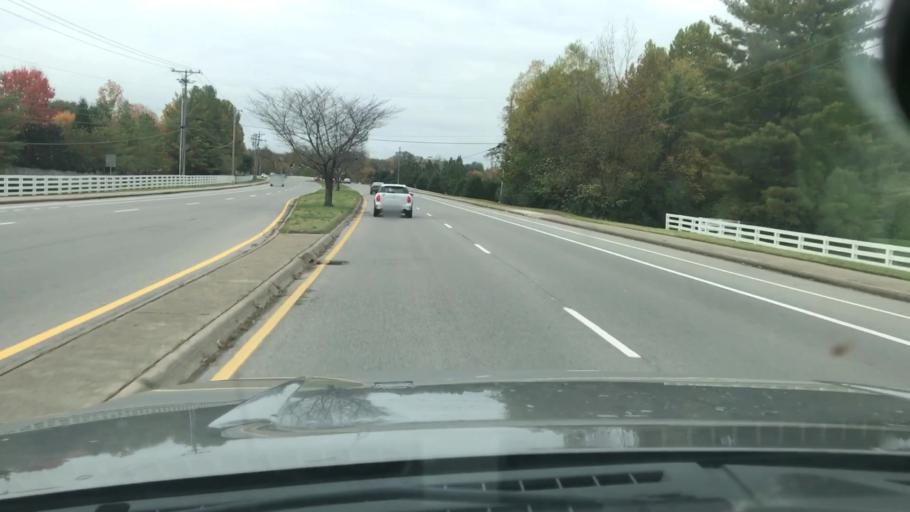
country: US
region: Tennessee
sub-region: Williamson County
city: Franklin
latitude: 35.9622
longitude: -86.8850
